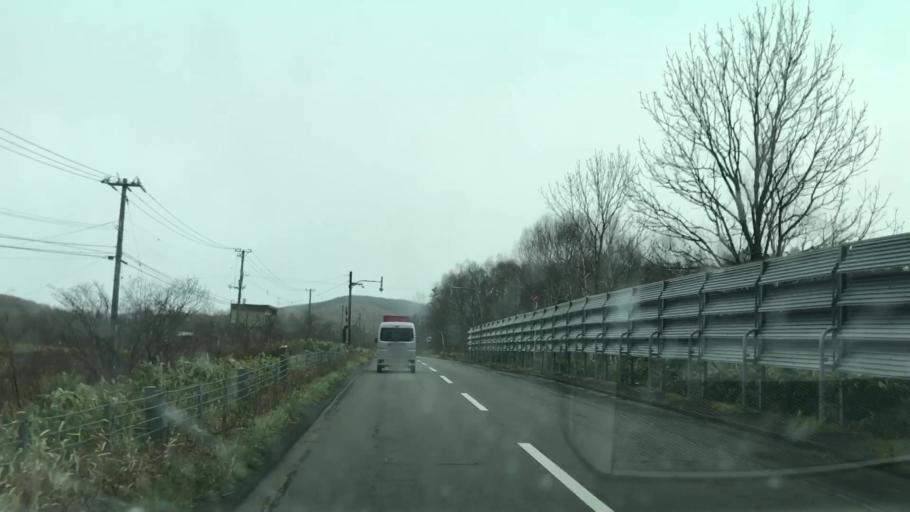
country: JP
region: Hokkaido
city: Yoichi
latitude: 43.3165
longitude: 140.5345
